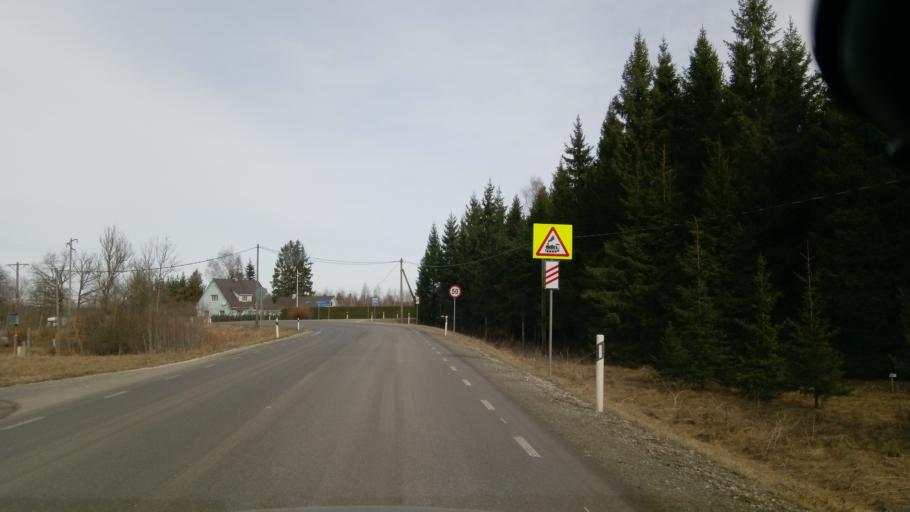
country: EE
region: Raplamaa
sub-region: Rapla vald
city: Rapla
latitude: 59.0173
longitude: 24.8378
